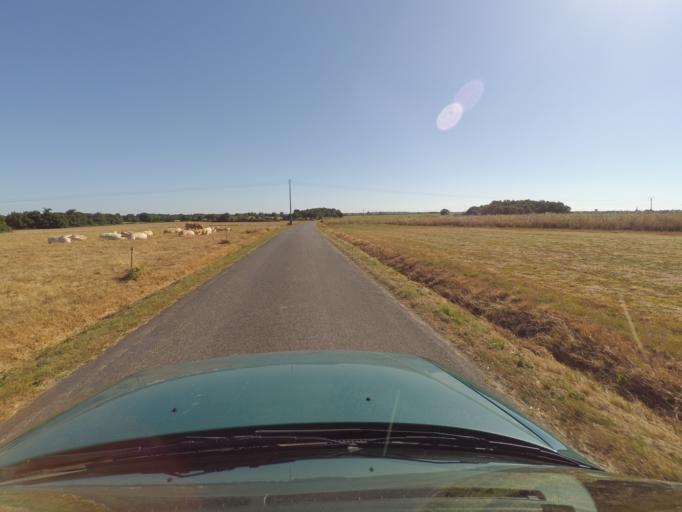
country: FR
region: Pays de la Loire
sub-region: Departement de la Loire-Atlantique
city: Maisdon-sur-Sevre
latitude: 47.0864
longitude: -1.3716
